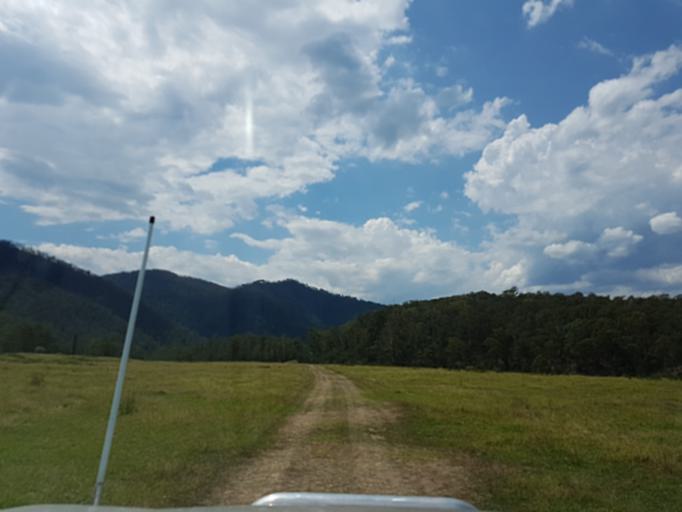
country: AU
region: Victoria
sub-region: East Gippsland
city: Lakes Entrance
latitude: -37.4002
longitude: 148.3339
